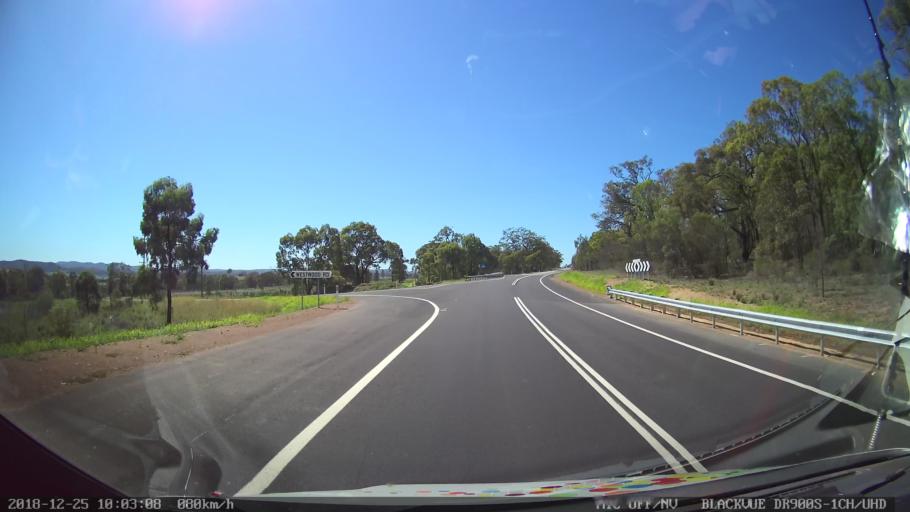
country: AU
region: New South Wales
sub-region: Upper Hunter Shire
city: Merriwa
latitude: -32.2255
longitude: 150.4688
